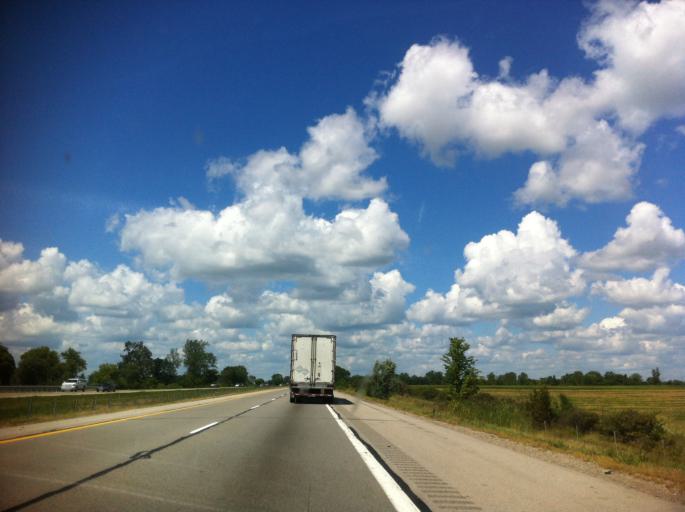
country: US
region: Michigan
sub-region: Monroe County
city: Dundee
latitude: 41.9863
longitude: -83.6782
